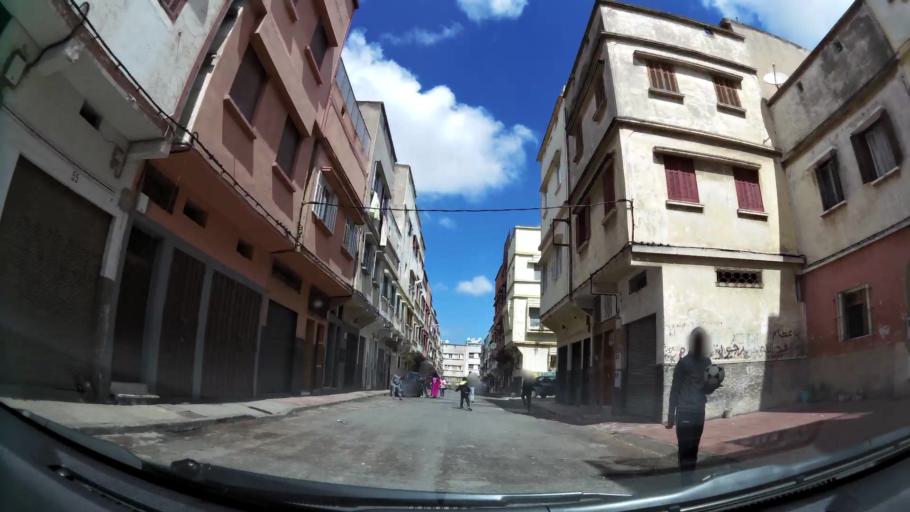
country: MA
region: Grand Casablanca
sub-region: Casablanca
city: Casablanca
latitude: 33.5582
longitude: -7.6066
